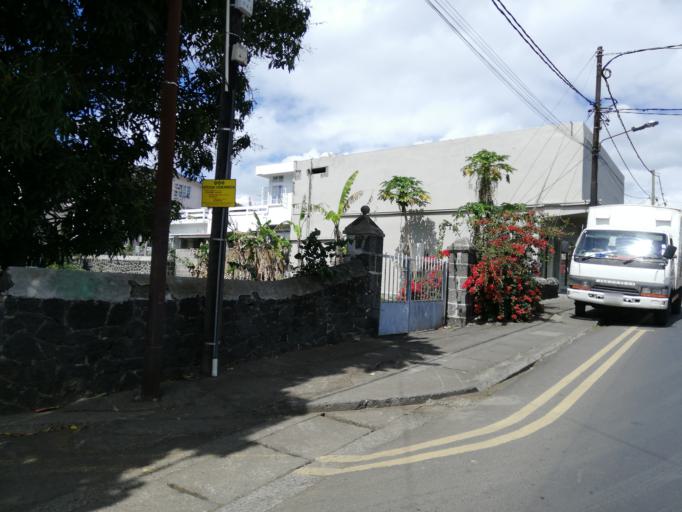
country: MU
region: Plaines Wilhems
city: Ebene
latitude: -20.2365
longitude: 57.4715
